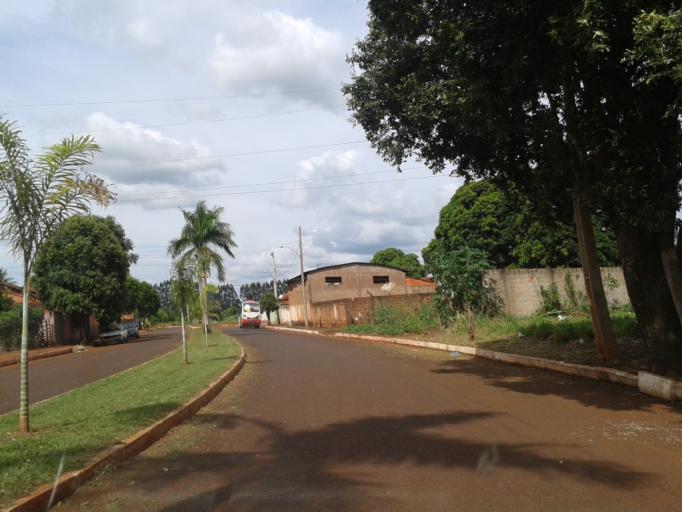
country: BR
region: Minas Gerais
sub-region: Centralina
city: Centralina
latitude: -18.5932
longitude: -49.1973
